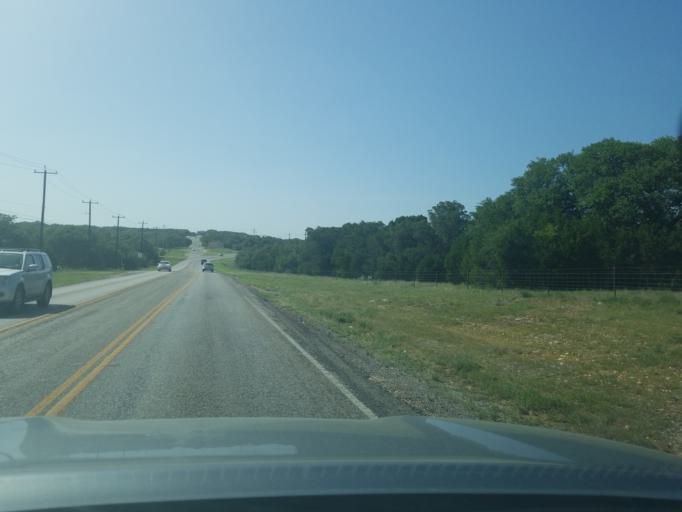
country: US
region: Texas
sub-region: Comal County
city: Garden Ridge
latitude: 29.6878
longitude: -98.3301
